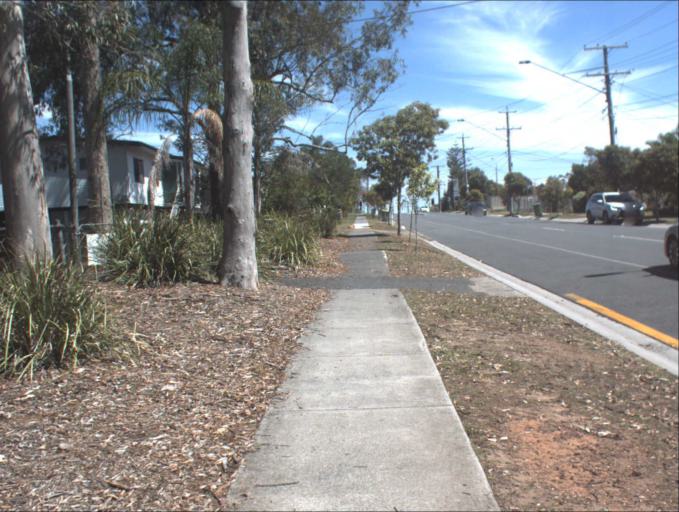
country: AU
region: Queensland
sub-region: Logan
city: Woodridge
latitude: -27.6268
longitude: 153.1040
